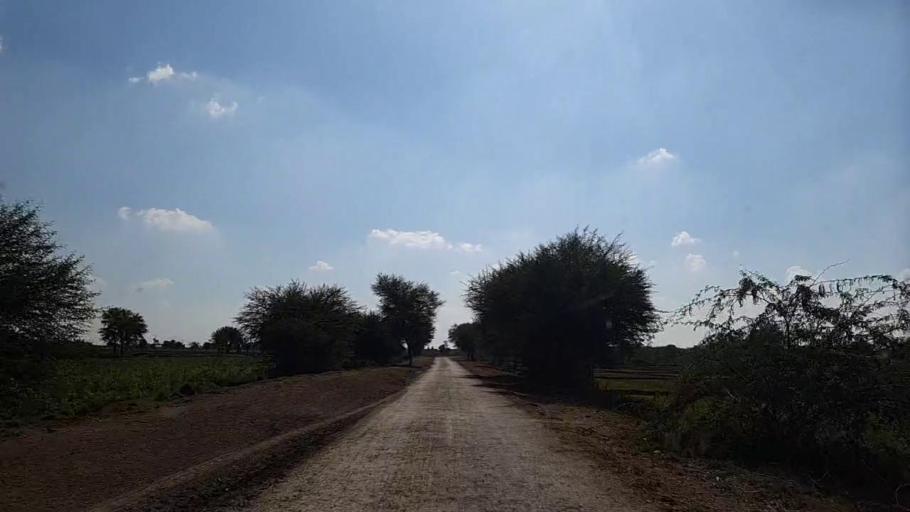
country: PK
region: Sindh
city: Pithoro
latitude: 25.6501
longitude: 69.4486
